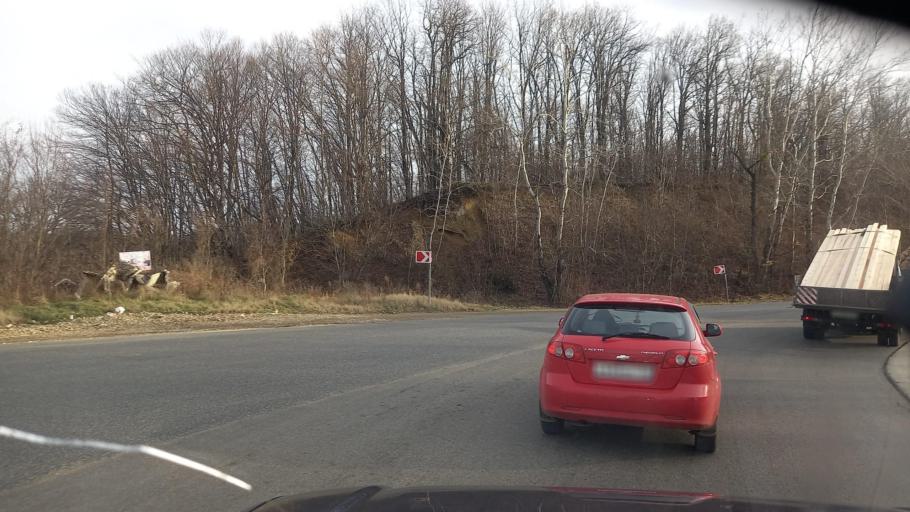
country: RU
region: Krasnodarskiy
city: Apsheronsk
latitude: 44.6053
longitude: 39.6209
